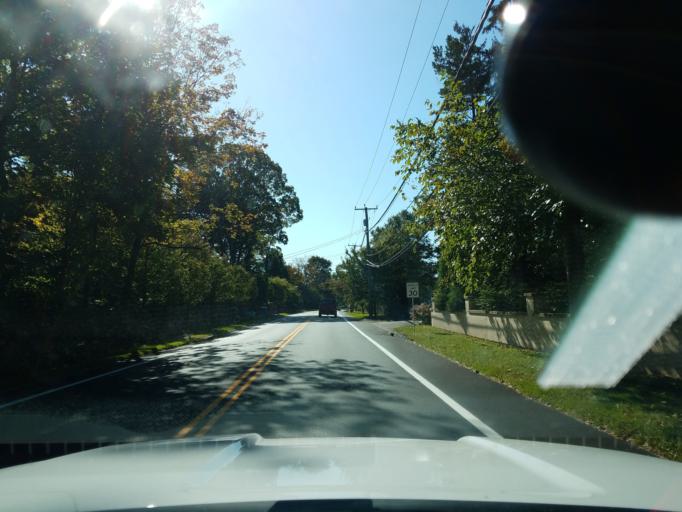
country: US
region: Connecticut
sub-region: Fairfield County
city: Cos Cob
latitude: 41.0560
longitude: -73.6170
